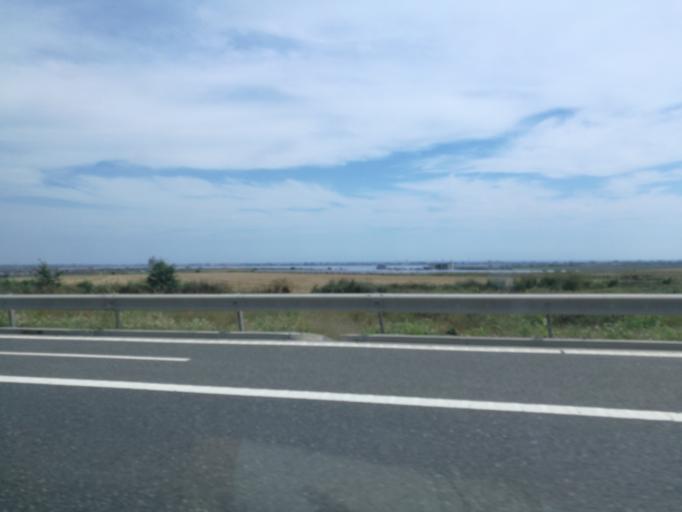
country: RO
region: Constanta
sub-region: Comuna Ovidiu
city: Ovidiu
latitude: 44.2335
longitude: 28.5496
